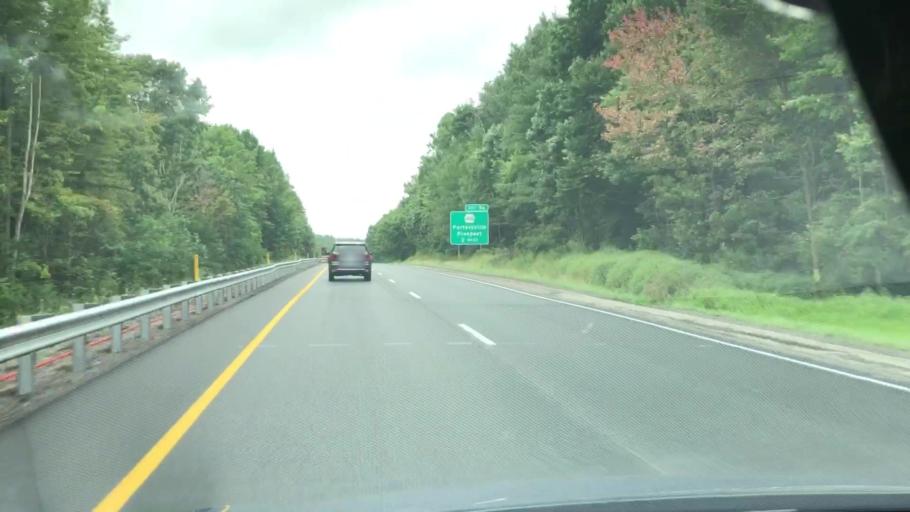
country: US
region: Pennsylvania
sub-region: Butler County
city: Prospect
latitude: 40.8945
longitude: -80.1210
